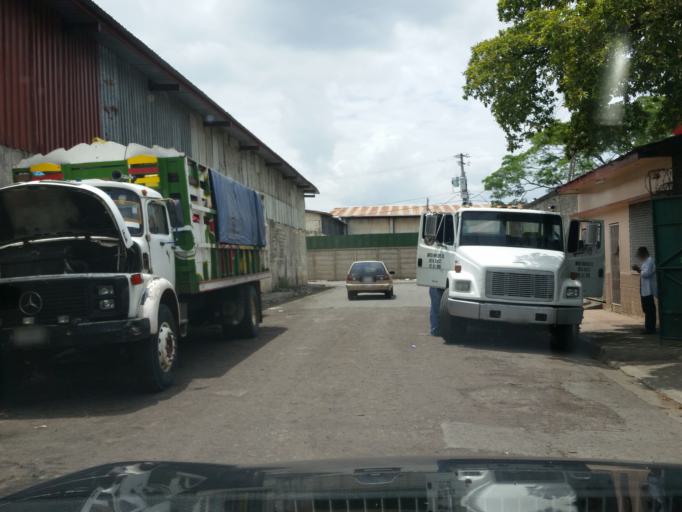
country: NI
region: Managua
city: Managua
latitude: 12.1531
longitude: -86.2617
